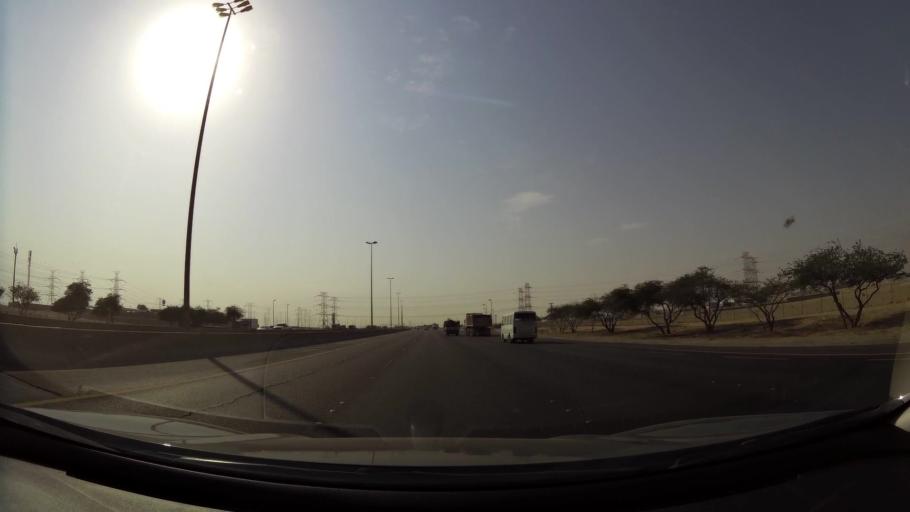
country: KW
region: Al Ahmadi
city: Al Ahmadi
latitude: 29.0088
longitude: 48.0940
